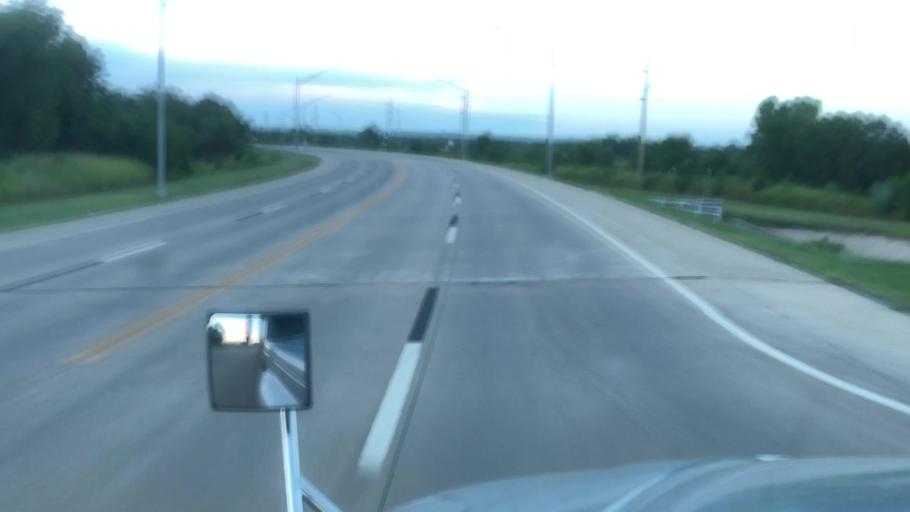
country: US
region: Oklahoma
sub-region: Kay County
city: Ponca City
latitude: 36.6880
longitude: -97.0679
